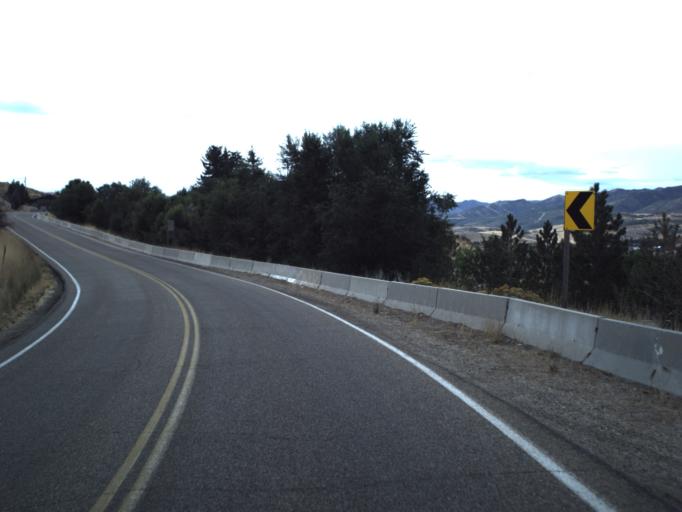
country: US
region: Utah
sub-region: Morgan County
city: Morgan
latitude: 40.9936
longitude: -111.6823
